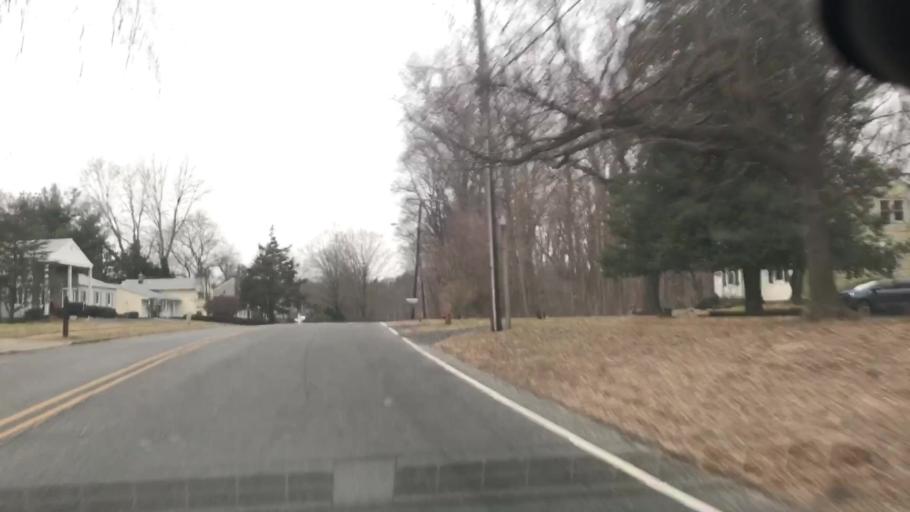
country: US
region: New Jersey
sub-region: Monmouth County
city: Fairview
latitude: 40.3724
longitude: -74.1026
